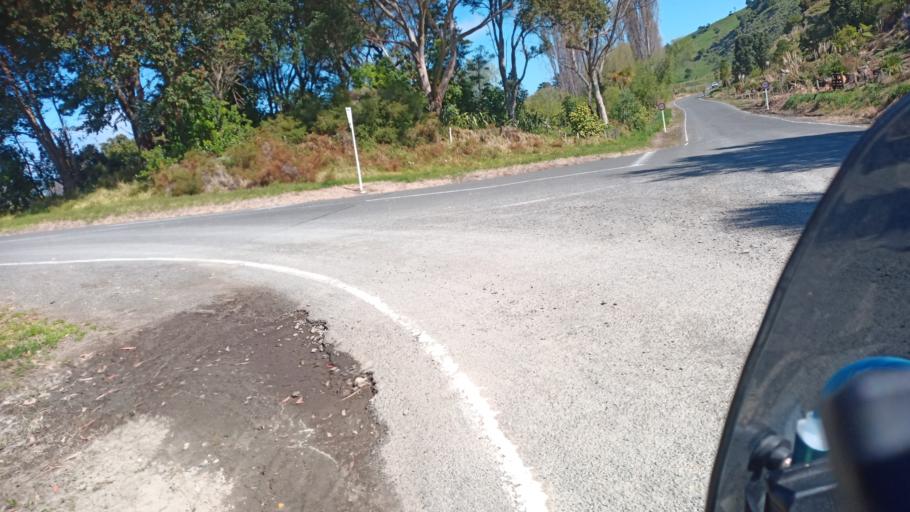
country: NZ
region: Gisborne
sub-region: Gisborne District
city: Gisborne
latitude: -39.0153
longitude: 177.8795
